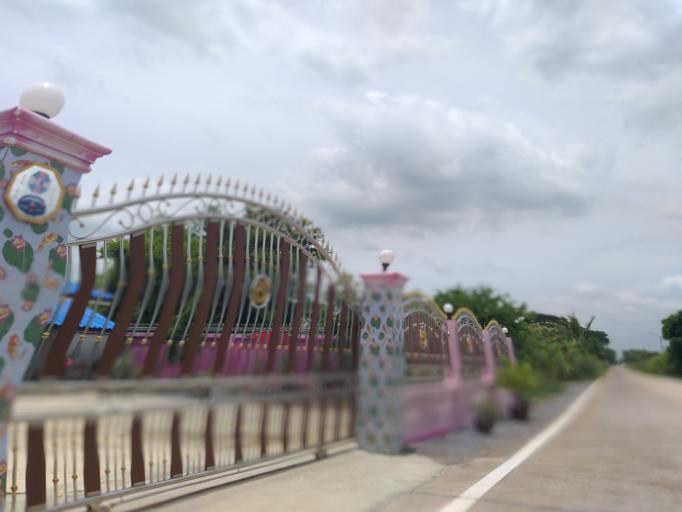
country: TH
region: Pathum Thani
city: Ban Lam Luk Ka
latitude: 13.9846
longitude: 100.8533
